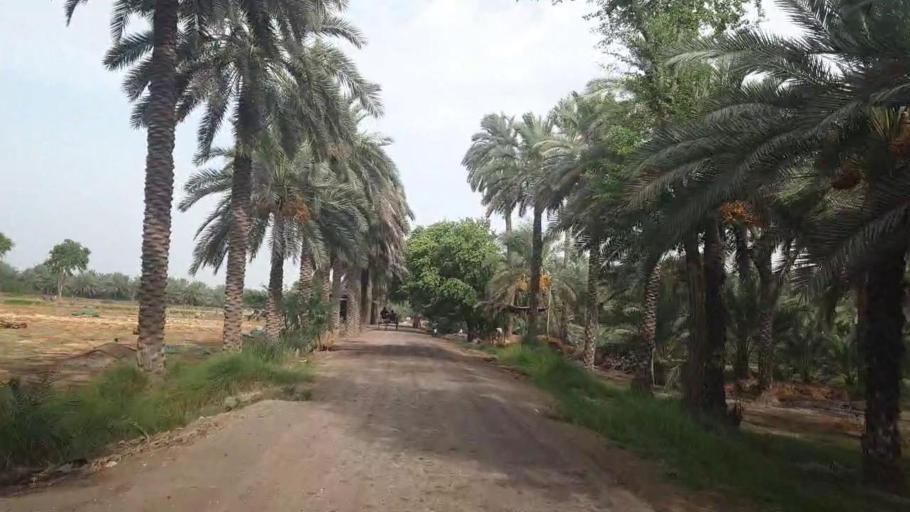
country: PK
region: Sindh
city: Sukkur
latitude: 27.6417
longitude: 68.8224
